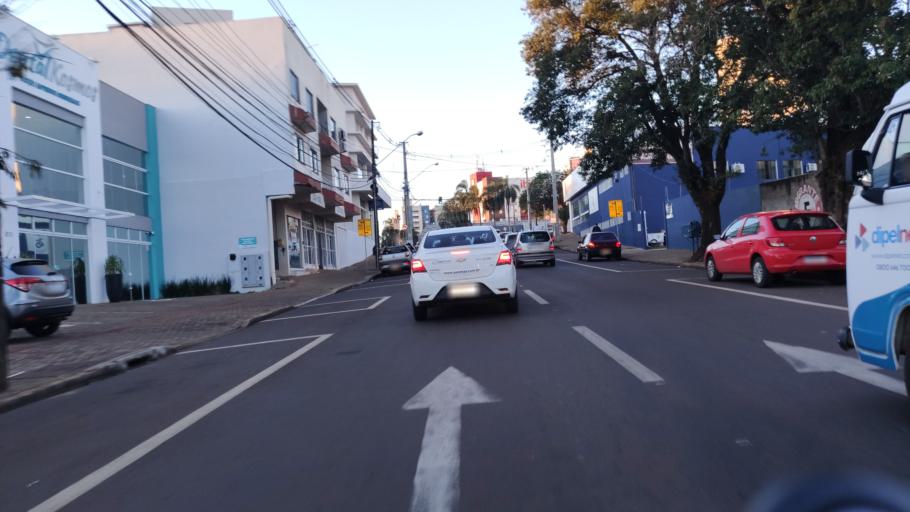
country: BR
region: Parana
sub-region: Cascavel
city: Cascavel
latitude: -24.9553
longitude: -53.4757
